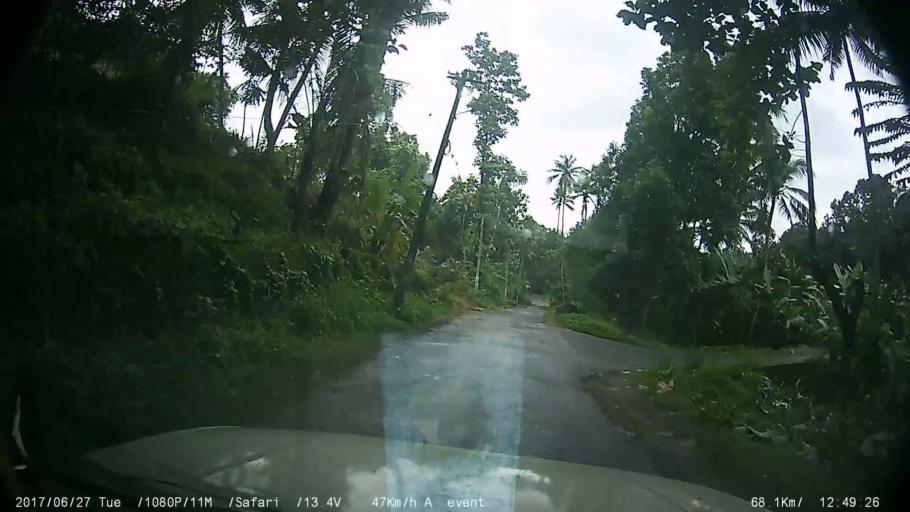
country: IN
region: Kerala
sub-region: Ernakulam
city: Piravam
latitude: 9.7808
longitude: 76.5266
